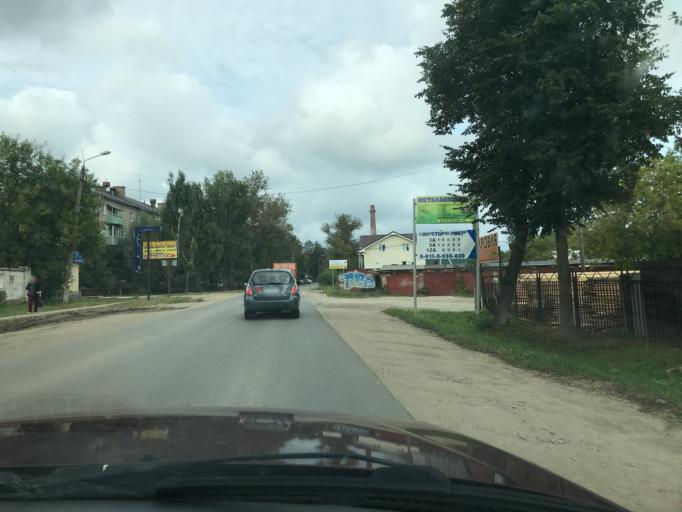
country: RU
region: Kaluga
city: Maloyaroslavets
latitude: 55.0016
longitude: 36.4713
